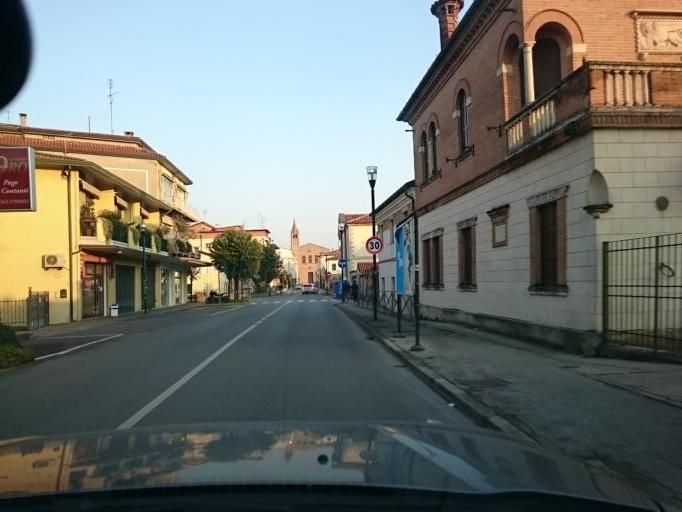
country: IT
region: Veneto
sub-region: Provincia di Padova
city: Abano Terme
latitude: 45.3613
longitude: 11.7873
